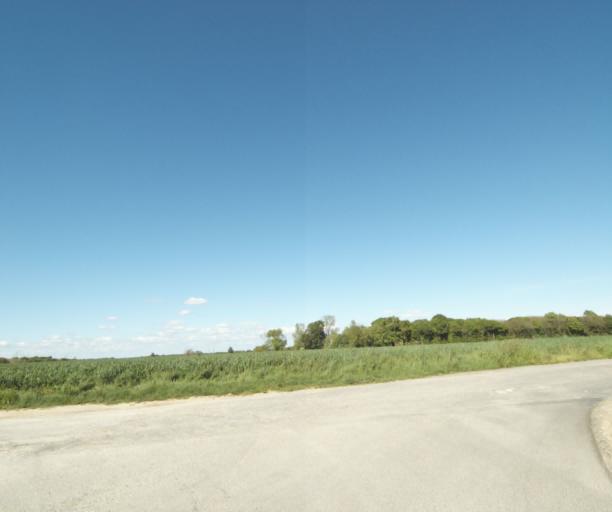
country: FR
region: Poitou-Charentes
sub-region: Departement de la Charente-Maritime
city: Saint-Georges-des-Coteaux
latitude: 45.7929
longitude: -0.7259
